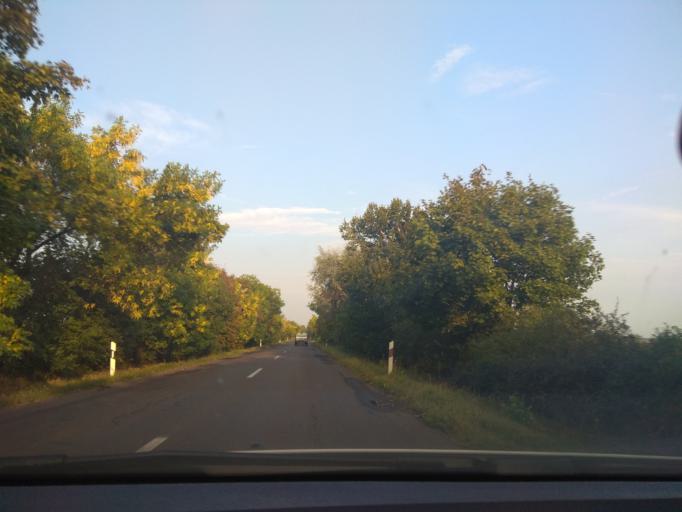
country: HU
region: Heves
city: Ostoros
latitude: 47.8262
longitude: 20.4708
